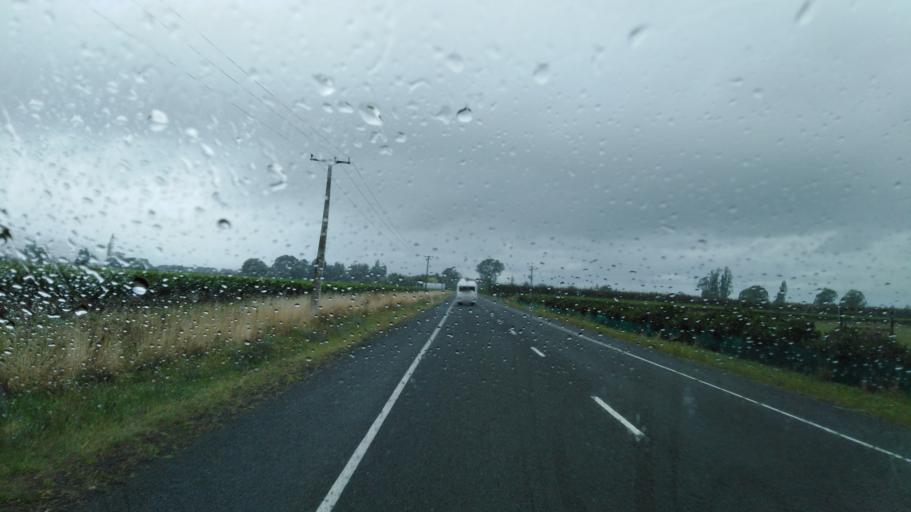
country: NZ
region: Marlborough
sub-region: Marlborough District
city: Blenheim
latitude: -41.4609
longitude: 173.9404
